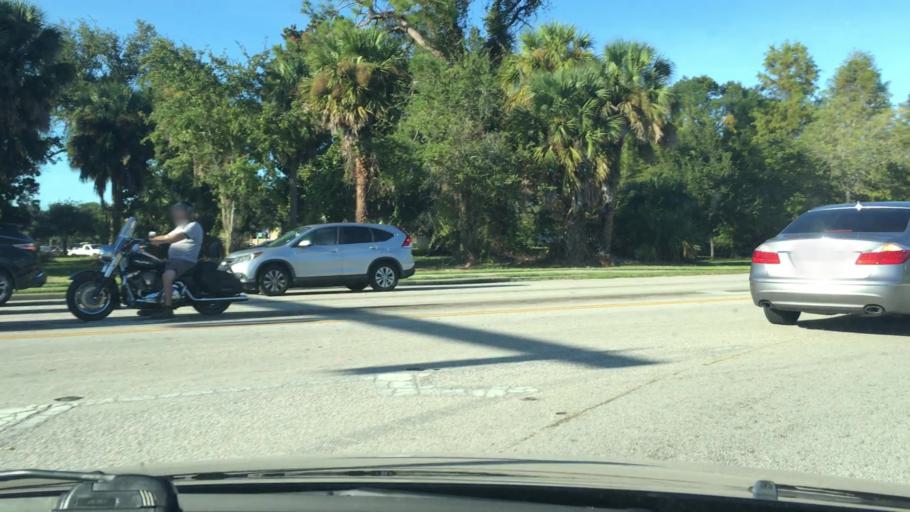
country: US
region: Florida
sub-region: Volusia County
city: Holly Hill
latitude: 29.2471
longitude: -81.0672
